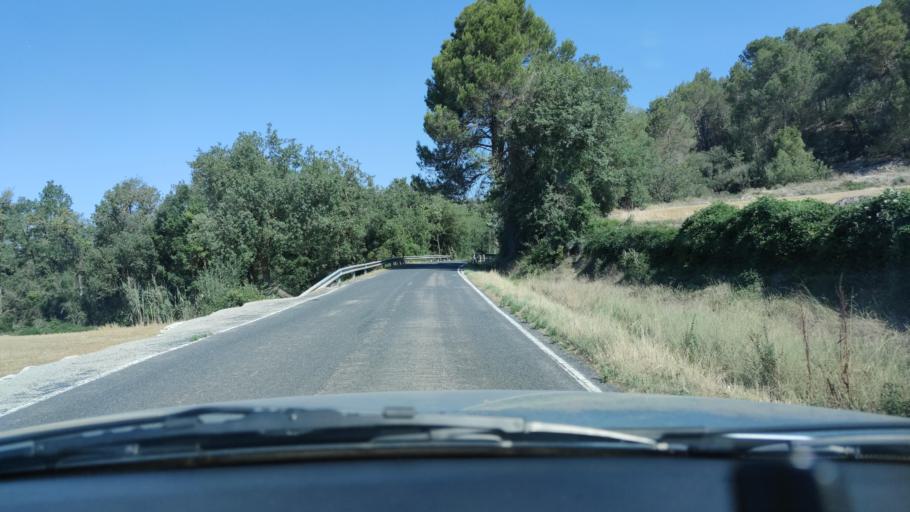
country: ES
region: Catalonia
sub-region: Provincia de Lleida
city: Sant Guim de Freixenet
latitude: 41.6706
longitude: 1.3632
